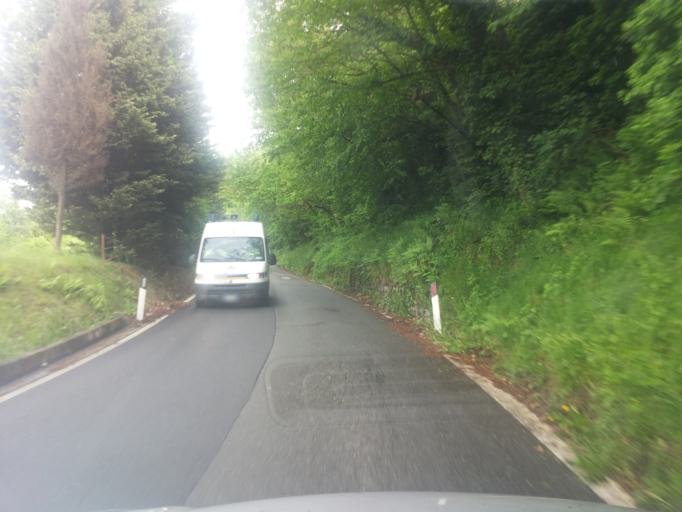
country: IT
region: Piedmont
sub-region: Provincia di Torino
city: Caravino
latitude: 45.3931
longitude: 7.9644
